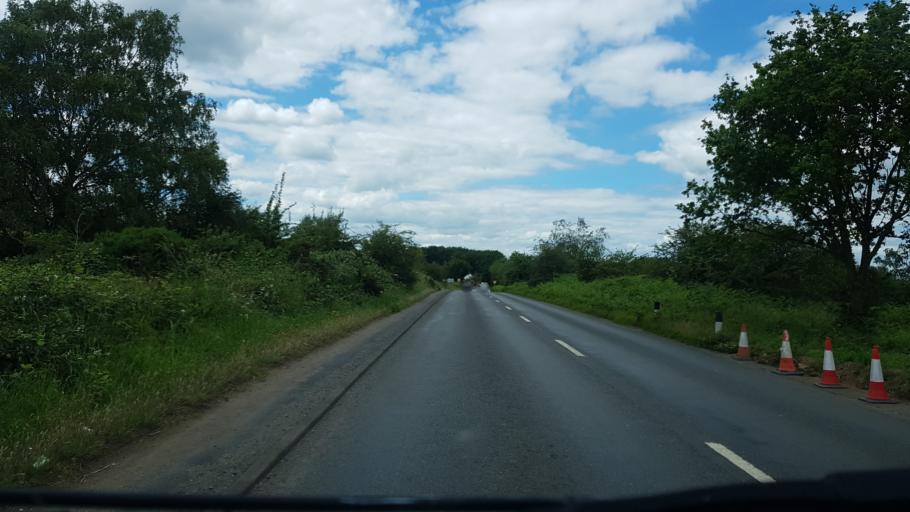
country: GB
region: England
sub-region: Worcestershire
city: Stourport-on-Severn
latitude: 52.3316
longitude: -2.2643
